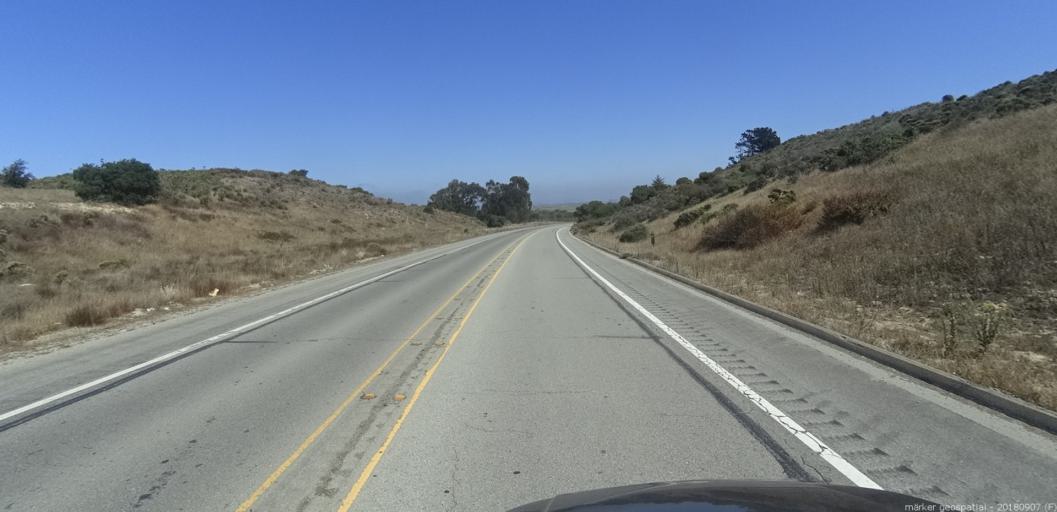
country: US
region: California
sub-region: Monterey County
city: Marina
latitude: 36.6741
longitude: -121.7514
